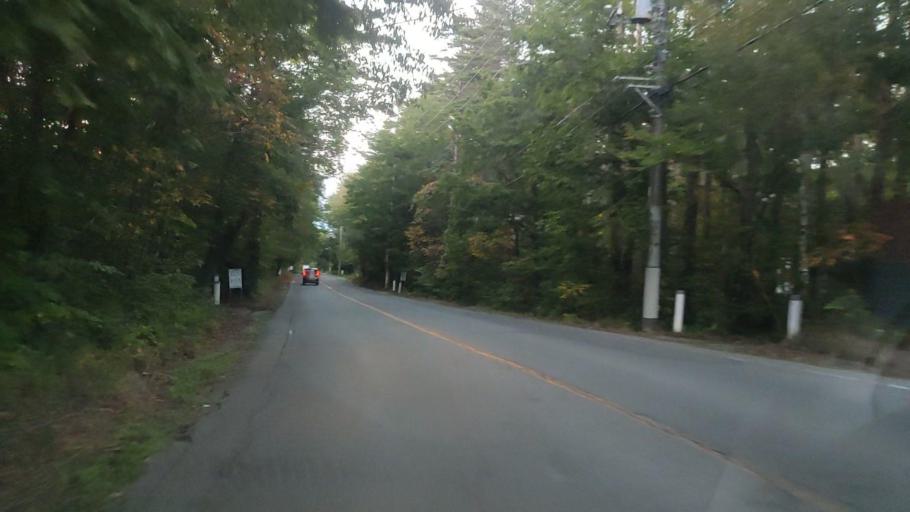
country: JP
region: Nagano
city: Komoro
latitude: 36.4448
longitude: 138.5797
